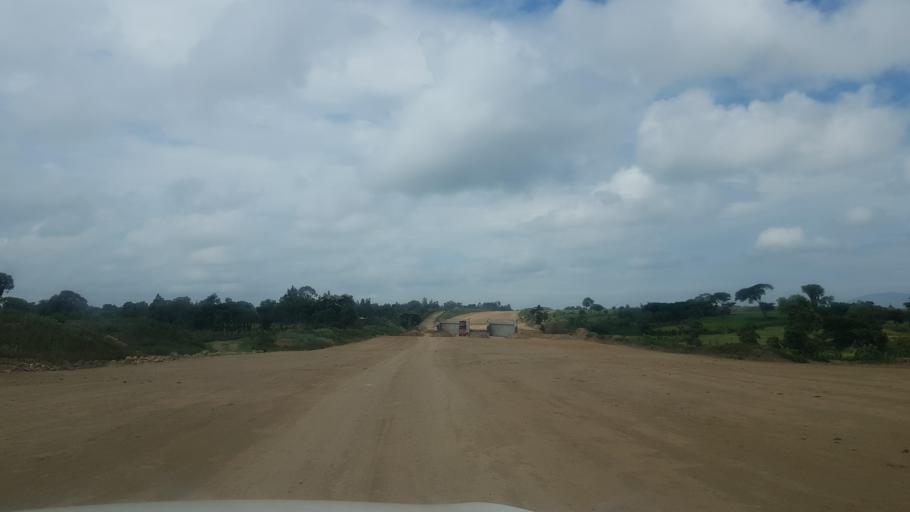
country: ET
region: Oromiya
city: Shashemene
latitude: 7.2515
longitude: 38.5915
